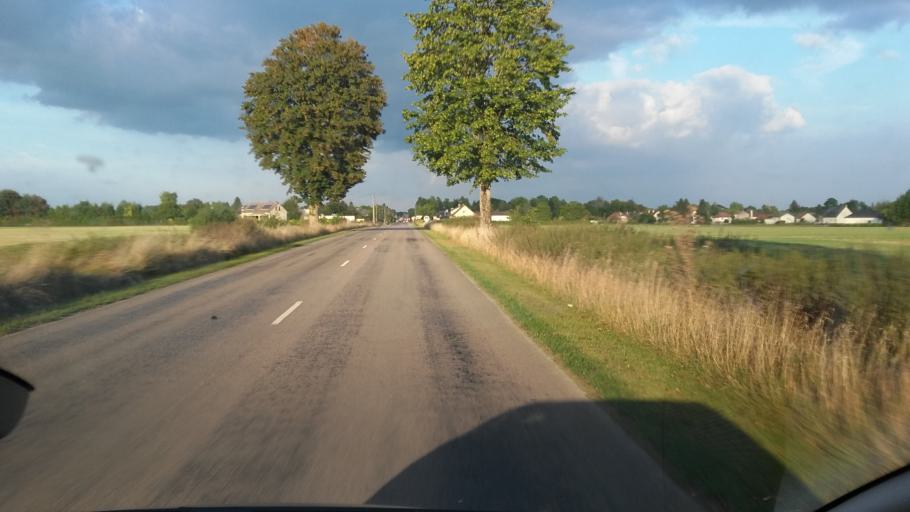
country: FR
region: Champagne-Ardenne
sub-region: Departement de la Marne
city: Fere-Champenoise
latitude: 48.7486
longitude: 3.9737
